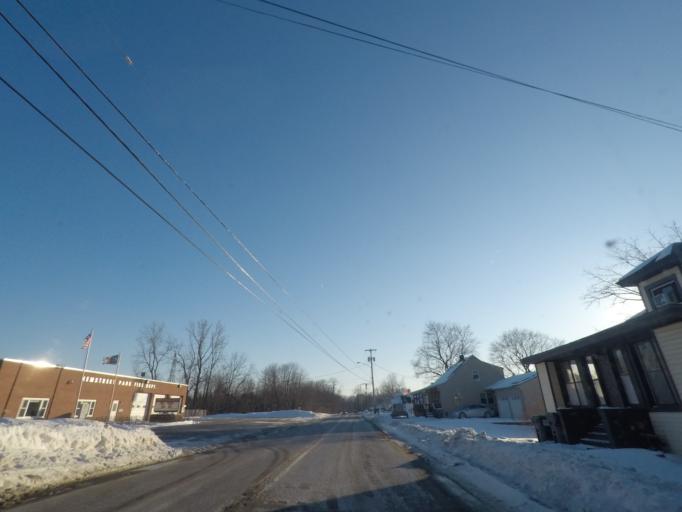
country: US
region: New York
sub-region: Saratoga County
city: Mechanicville
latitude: 42.9005
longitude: -73.6780
